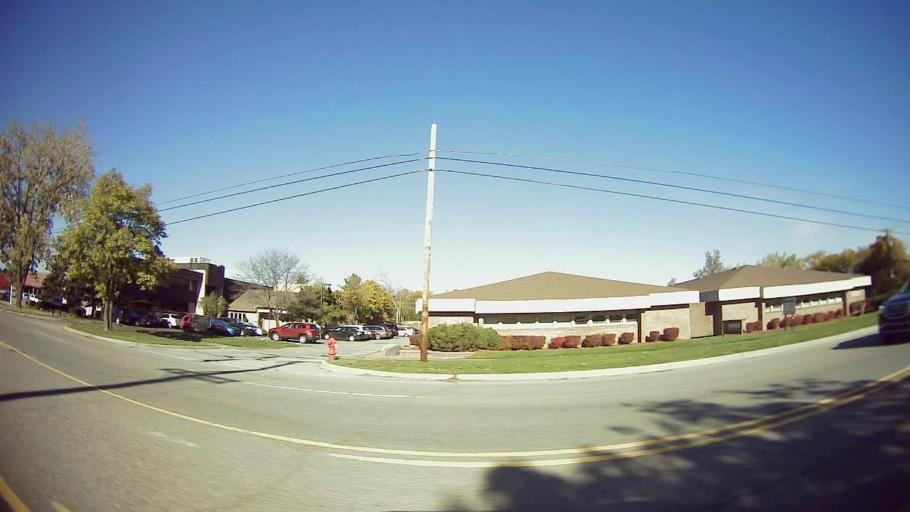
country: US
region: Michigan
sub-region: Oakland County
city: West Bloomfield Township
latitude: 42.5430
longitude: -83.3573
